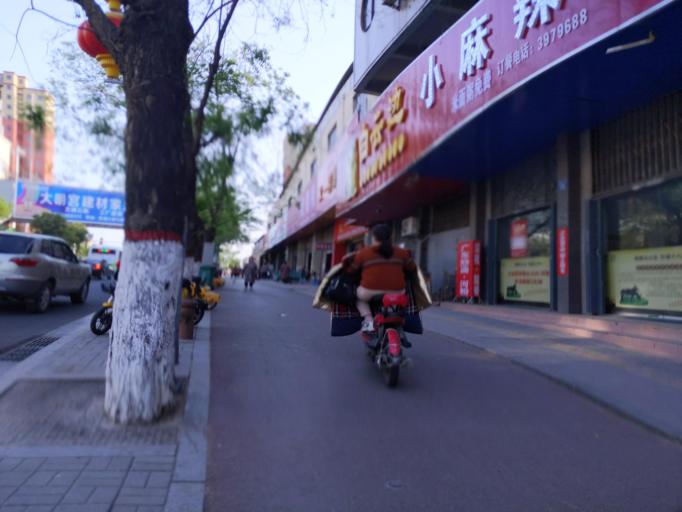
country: CN
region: Henan Sheng
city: Puyang Chengguanzhen
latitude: 35.6993
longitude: 115.0161
